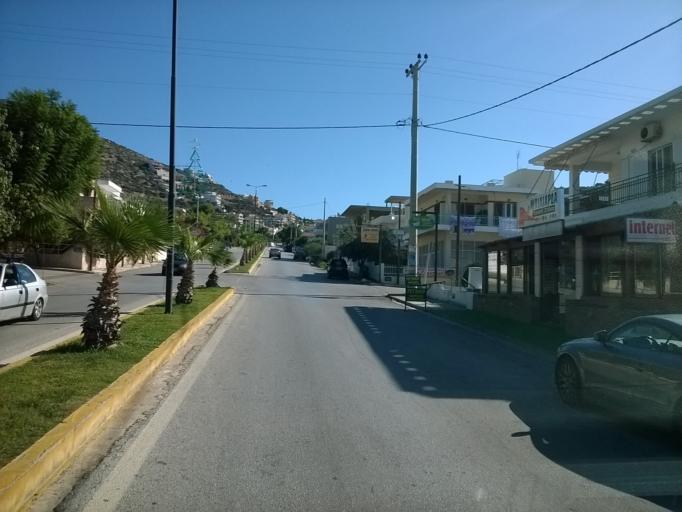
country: GR
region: Attica
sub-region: Nomarchia Anatolikis Attikis
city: Saronida
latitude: 37.7472
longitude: 23.9151
